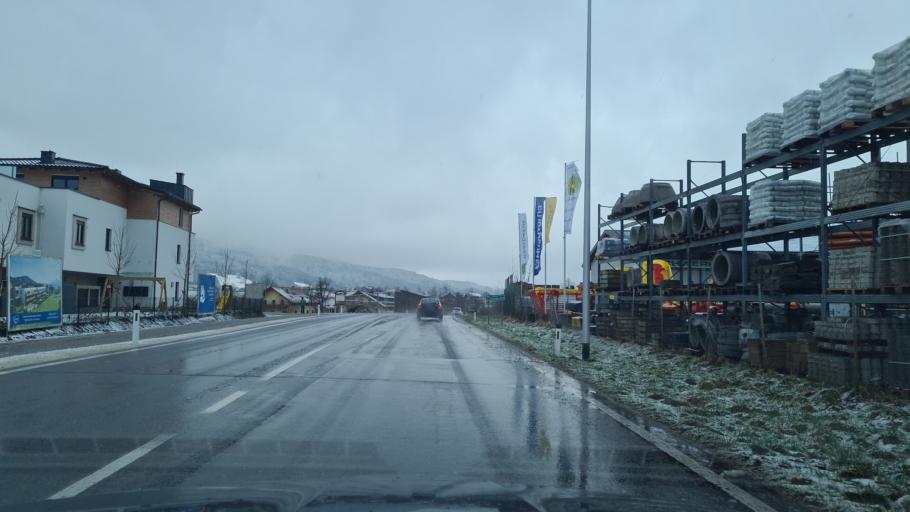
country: AT
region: Upper Austria
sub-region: Politischer Bezirk Vocklabruck
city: Zell am Moos
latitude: 47.8723
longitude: 13.3228
